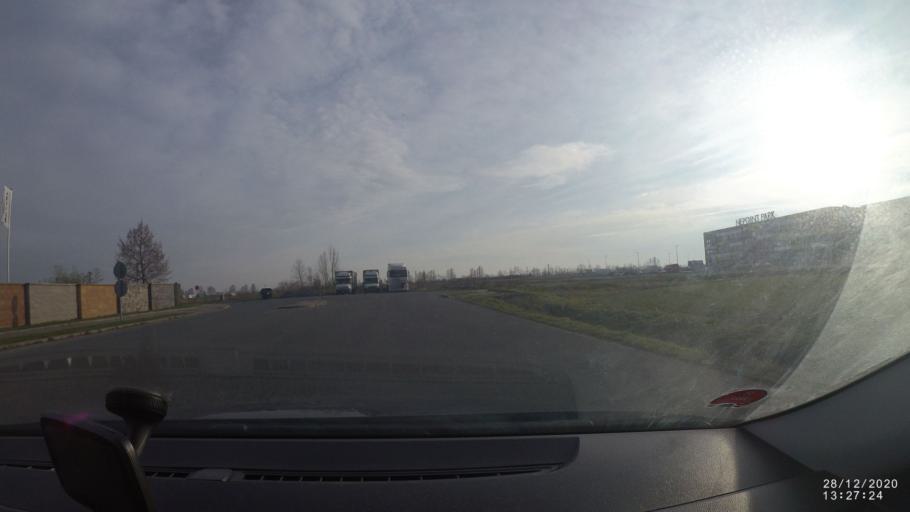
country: CZ
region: Central Bohemia
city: Jirny
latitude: 50.1267
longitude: 14.7127
